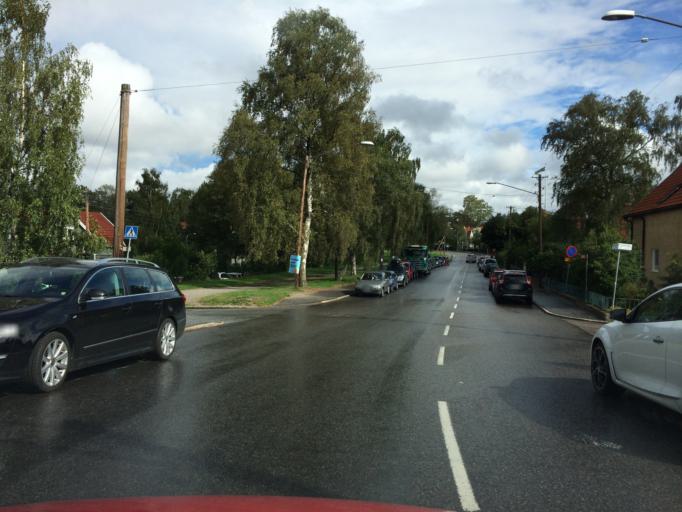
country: SE
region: Stockholm
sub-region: Huddinge Kommun
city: Segeltorp
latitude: 59.3011
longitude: 17.9581
